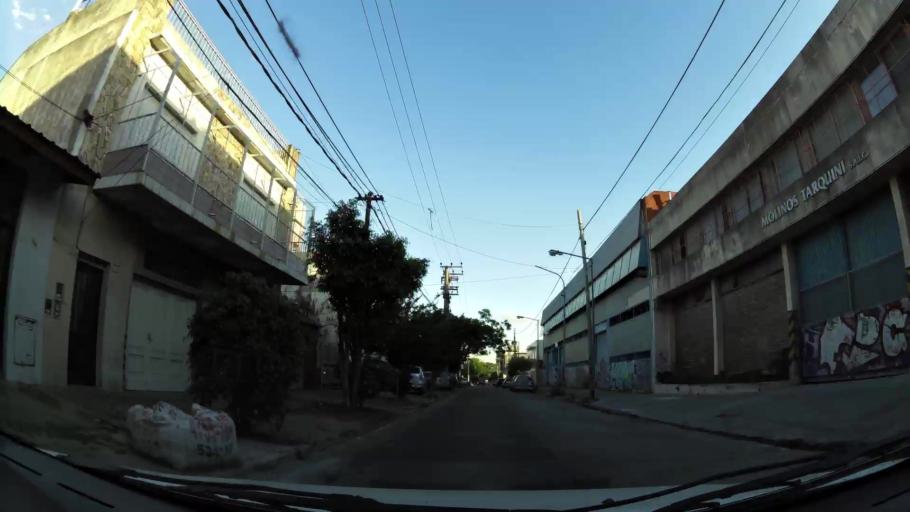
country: AR
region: Buenos Aires
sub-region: Partido de General San Martin
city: General San Martin
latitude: -34.5682
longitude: -58.5250
